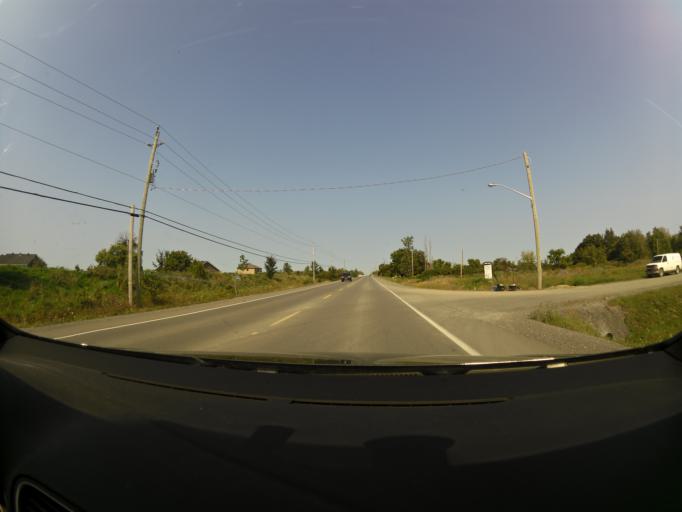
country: CA
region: Ontario
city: Bells Corners
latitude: 45.3100
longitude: -75.9928
